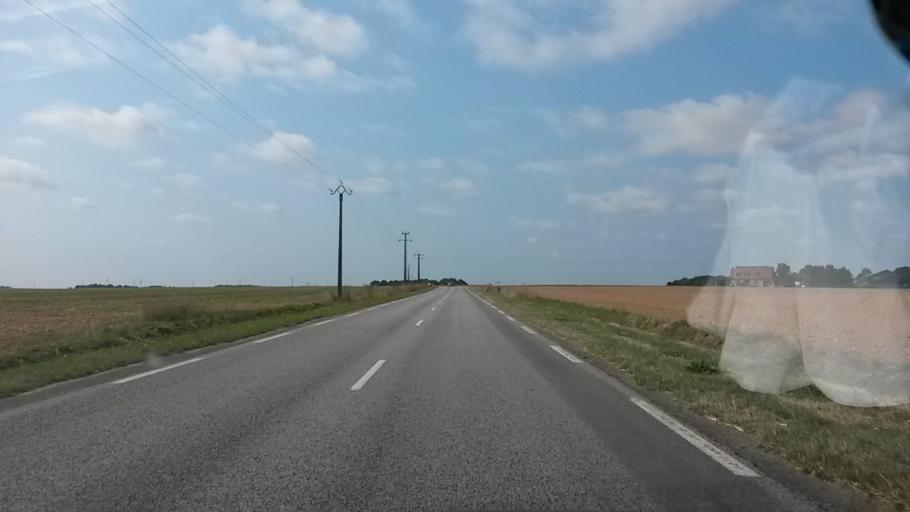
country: FR
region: Haute-Normandie
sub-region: Departement de l'Eure
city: Tillieres-sur-Avre
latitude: 48.8068
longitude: 1.0005
